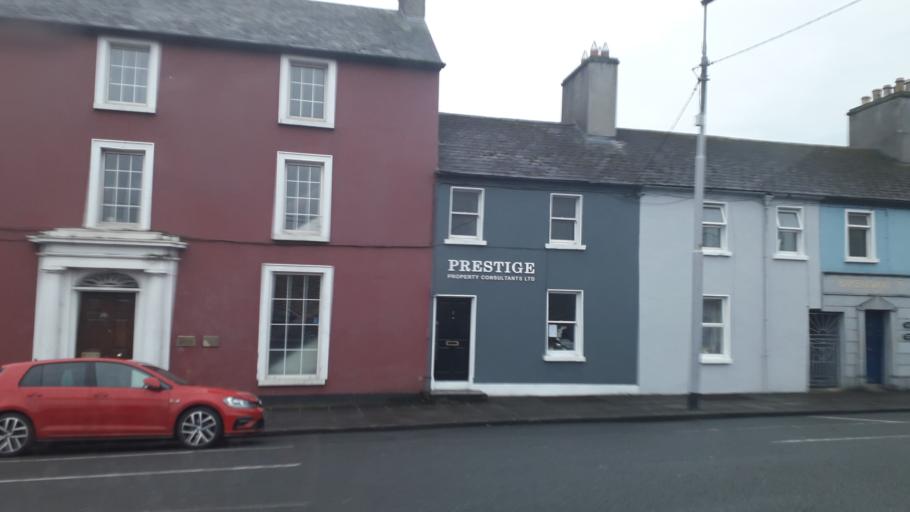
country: IE
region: Leinster
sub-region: An Longfort
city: Longford
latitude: 53.7310
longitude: -7.8010
